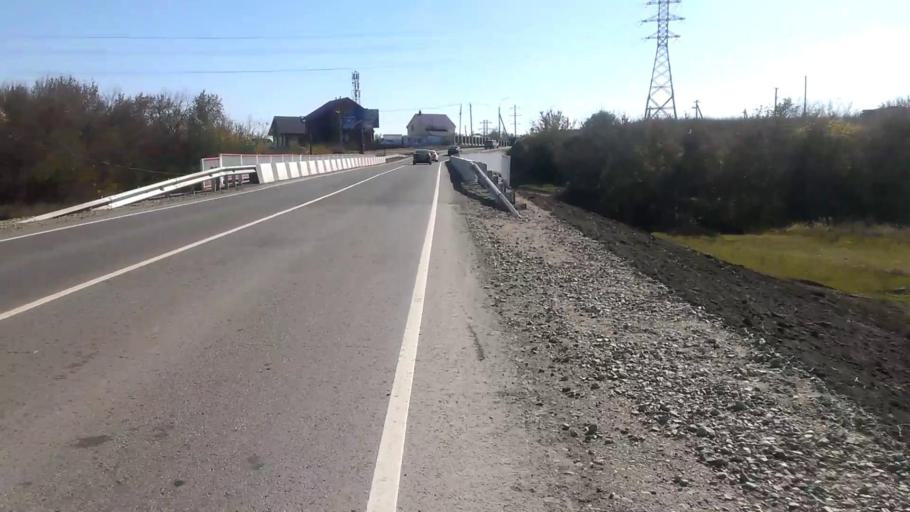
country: RU
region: Altai Krai
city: Sannikovo
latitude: 53.3203
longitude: 83.9437
